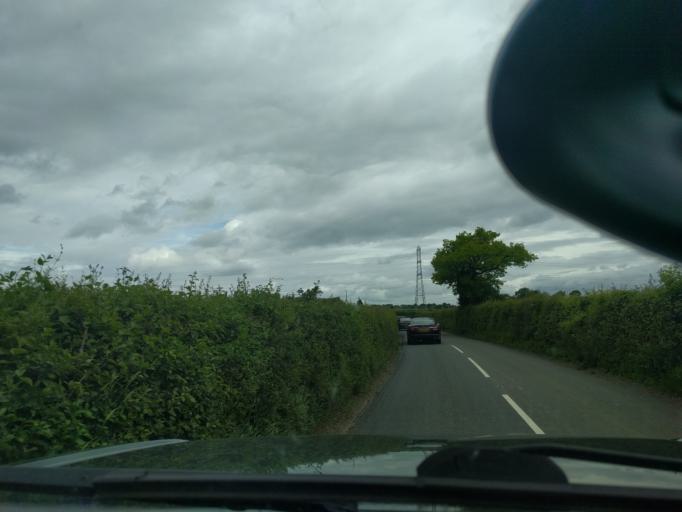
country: GB
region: England
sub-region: Wiltshire
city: Box
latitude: 51.3932
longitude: -2.2322
